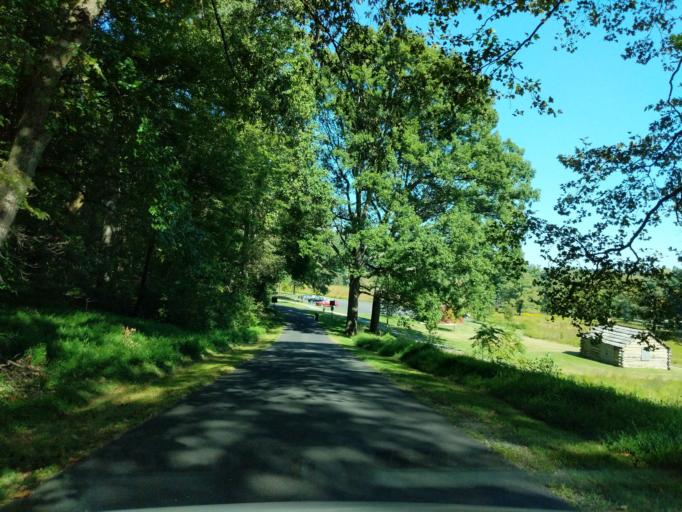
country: US
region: Pennsylvania
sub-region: Chester County
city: Chesterbrook
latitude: 40.0927
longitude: -75.4486
